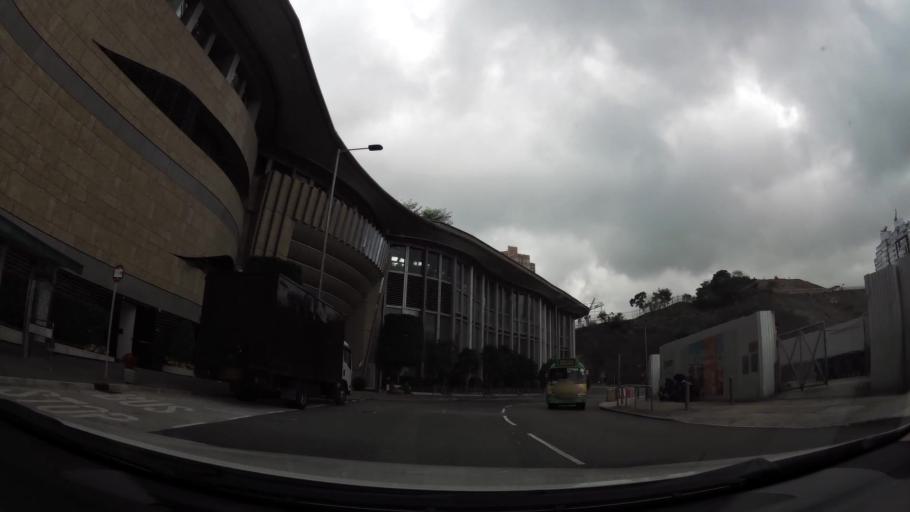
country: HK
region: Kowloon City
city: Kowloon
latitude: 22.3110
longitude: 114.1823
